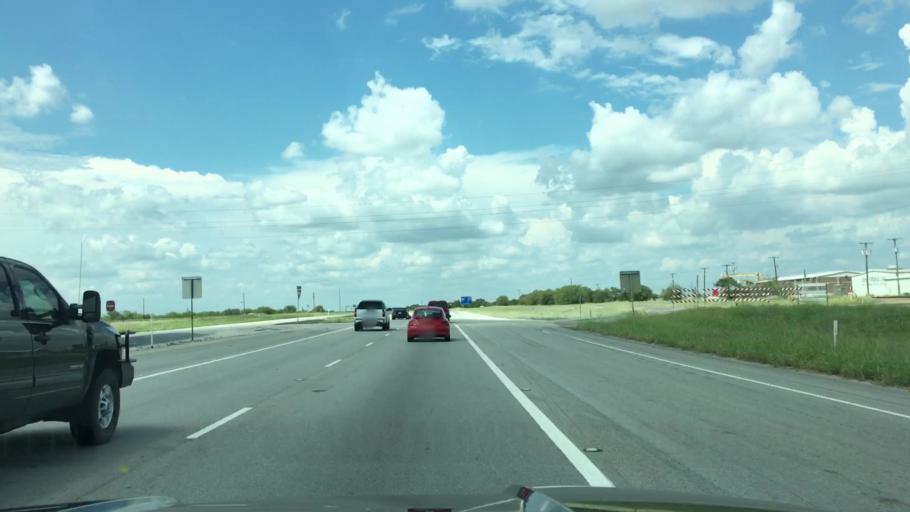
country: US
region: Texas
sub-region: Wise County
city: Rhome
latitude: 33.0354
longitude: -97.4523
